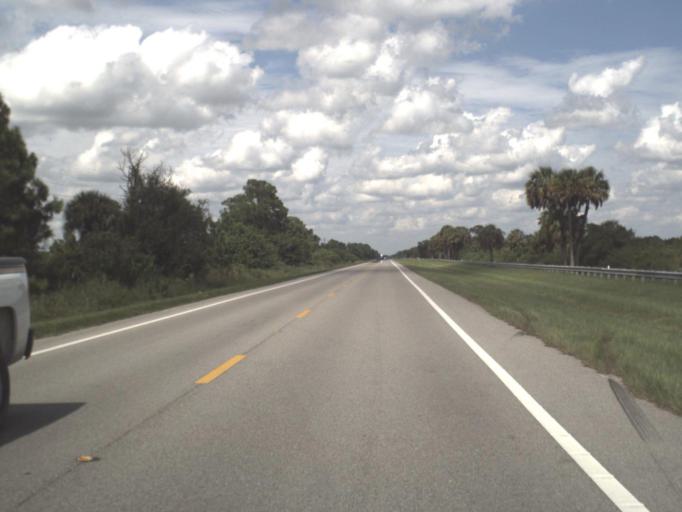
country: US
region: Florida
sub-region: Collier County
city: Immokalee
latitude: 26.3211
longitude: -81.3430
